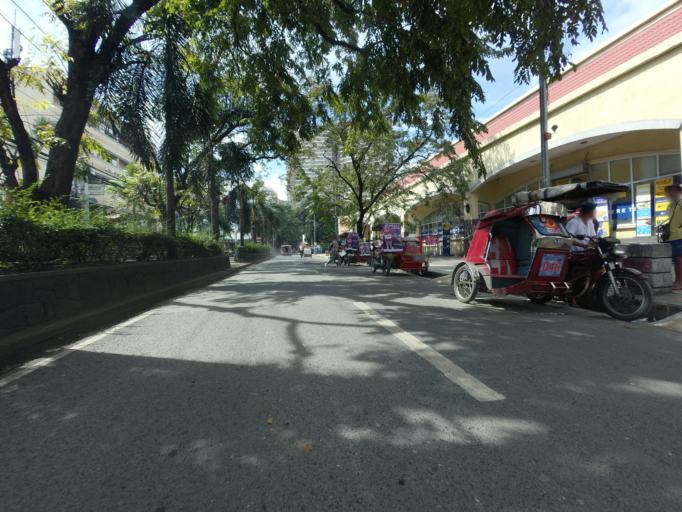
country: PH
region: Metro Manila
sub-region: San Juan
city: San Juan
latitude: 14.5815
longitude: 121.0119
